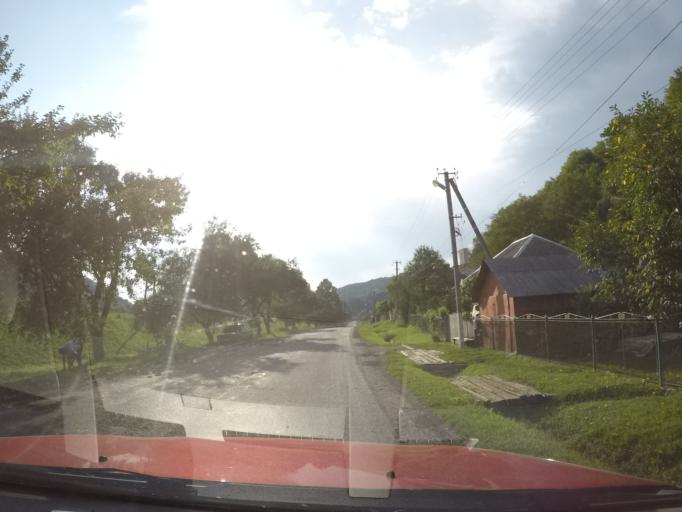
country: UA
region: Zakarpattia
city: Velykyi Bereznyi
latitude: 48.9517
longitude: 22.5359
